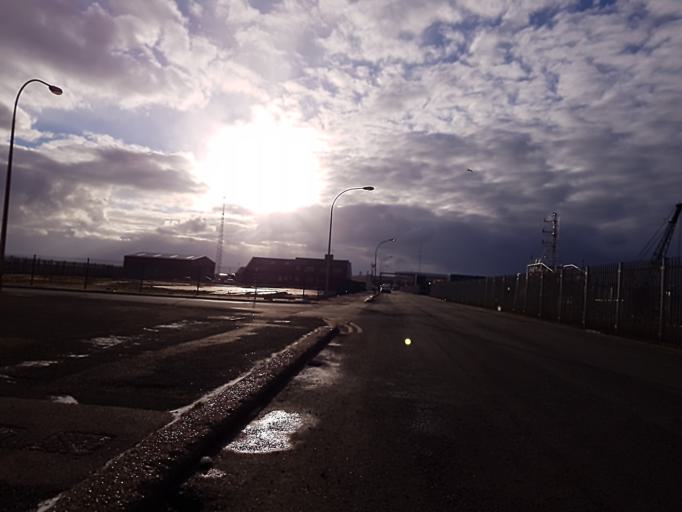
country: GB
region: England
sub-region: North East Lincolnshire
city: Grimsby
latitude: 53.5804
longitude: -0.0603
